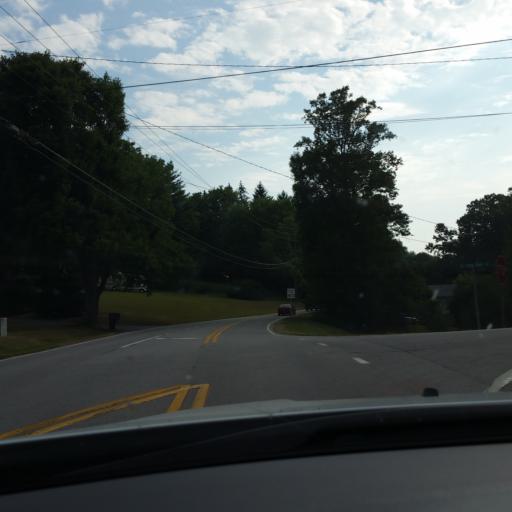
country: US
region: North Carolina
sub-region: Buncombe County
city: Bent Creek
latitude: 35.5259
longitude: -82.6795
